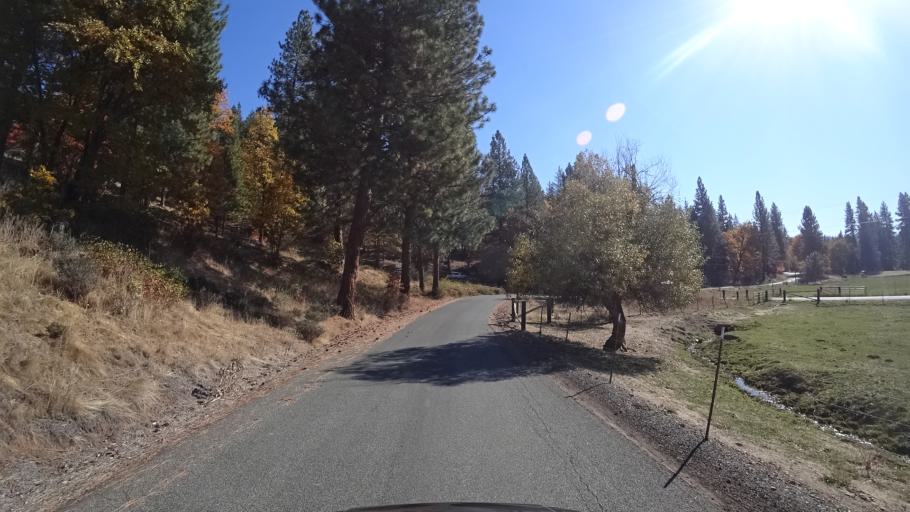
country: US
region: California
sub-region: Siskiyou County
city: Yreka
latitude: 41.5821
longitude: -122.9585
